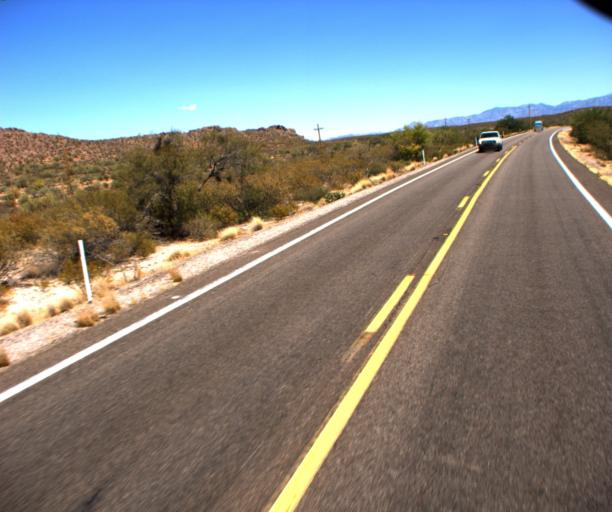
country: US
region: Arizona
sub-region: Pima County
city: Catalina
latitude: 32.6549
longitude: -111.0367
